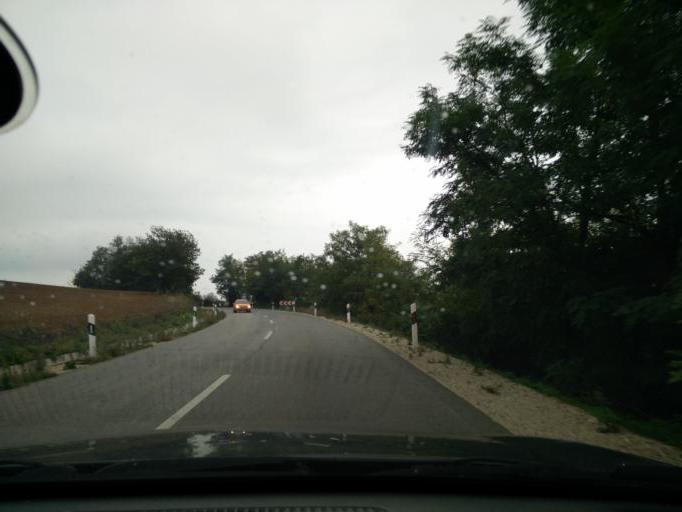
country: HU
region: Komarom-Esztergom
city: Bajna
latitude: 47.6592
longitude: 18.6039
